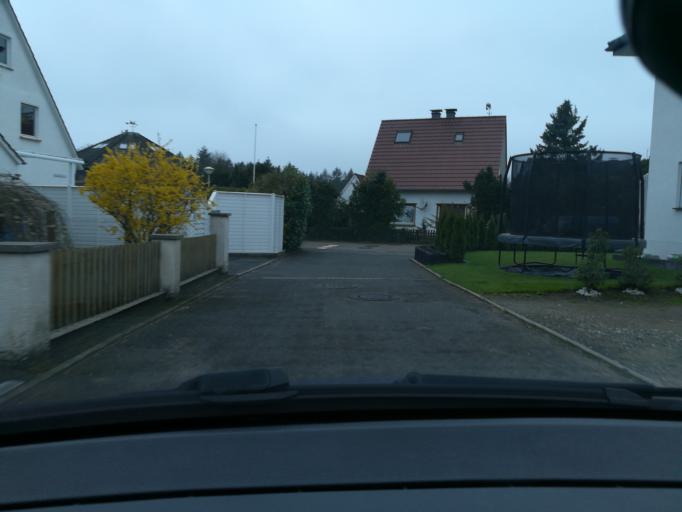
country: DE
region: North Rhine-Westphalia
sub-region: Regierungsbezirk Detmold
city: Oerlinghausen
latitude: 51.9317
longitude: 8.6311
